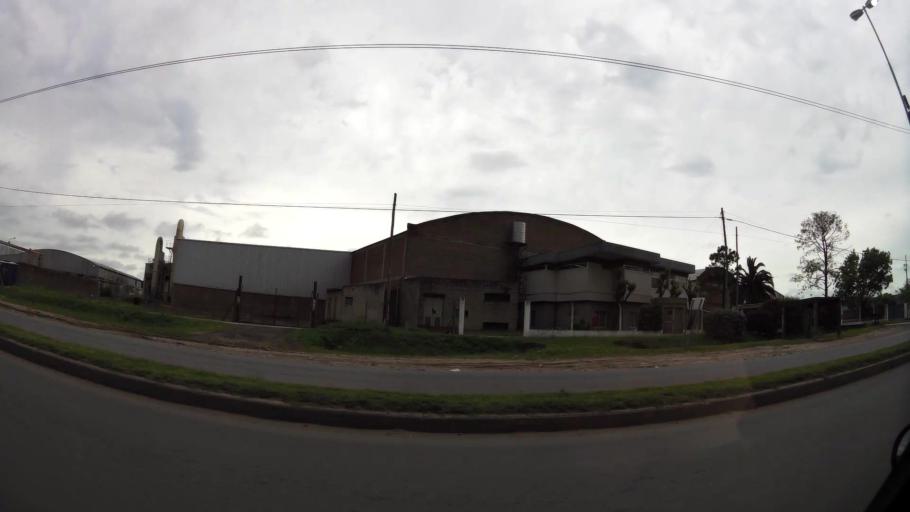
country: AR
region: Buenos Aires
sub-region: Partido de Quilmes
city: Quilmes
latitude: -34.7817
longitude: -58.2792
